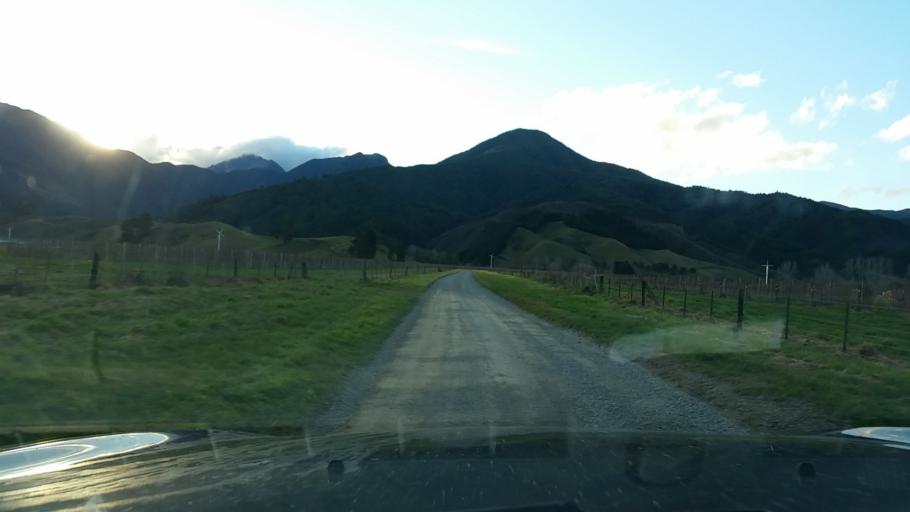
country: NZ
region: Marlborough
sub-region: Marlborough District
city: Blenheim
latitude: -41.5127
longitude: 173.5845
